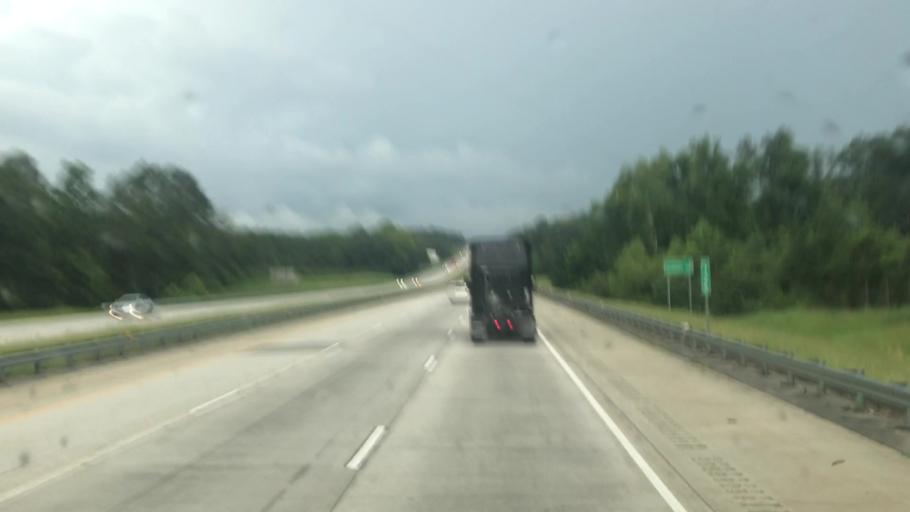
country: US
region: Georgia
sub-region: Dooly County
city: Unadilla
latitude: 32.3244
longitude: -83.7657
